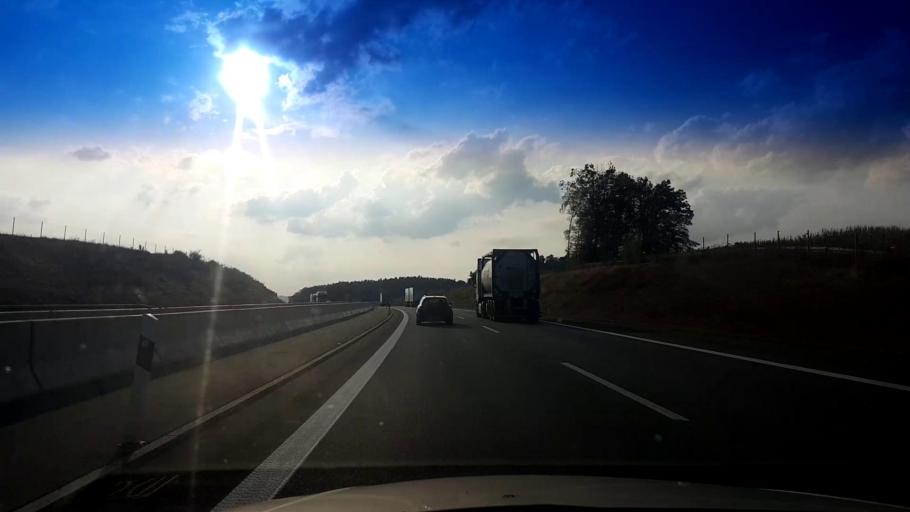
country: DE
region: Bavaria
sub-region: Upper Franconia
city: Neudrossenfeld
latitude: 50.0391
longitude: 11.5088
